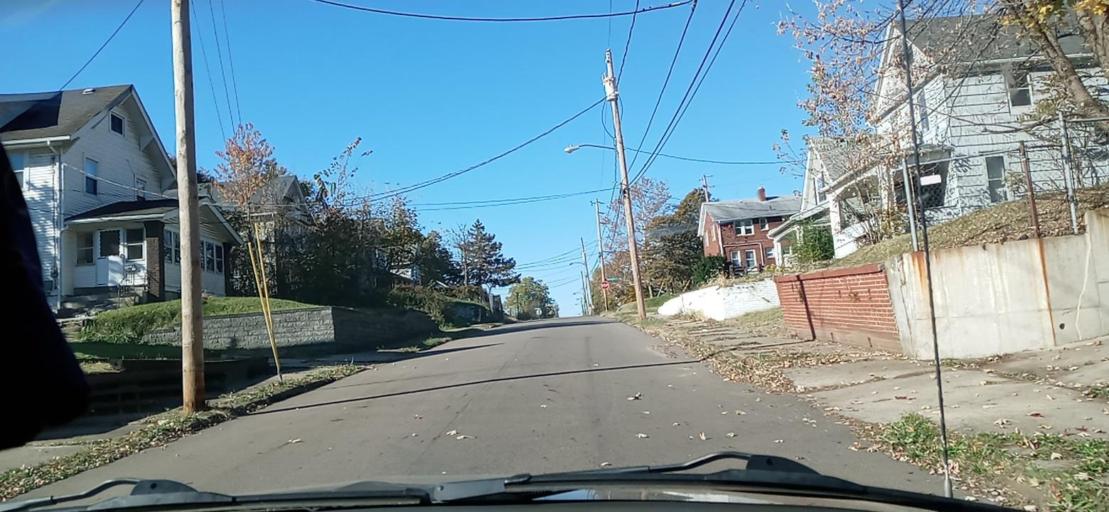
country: US
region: Ohio
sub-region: Summit County
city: Akron
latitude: 41.0596
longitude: -81.5334
